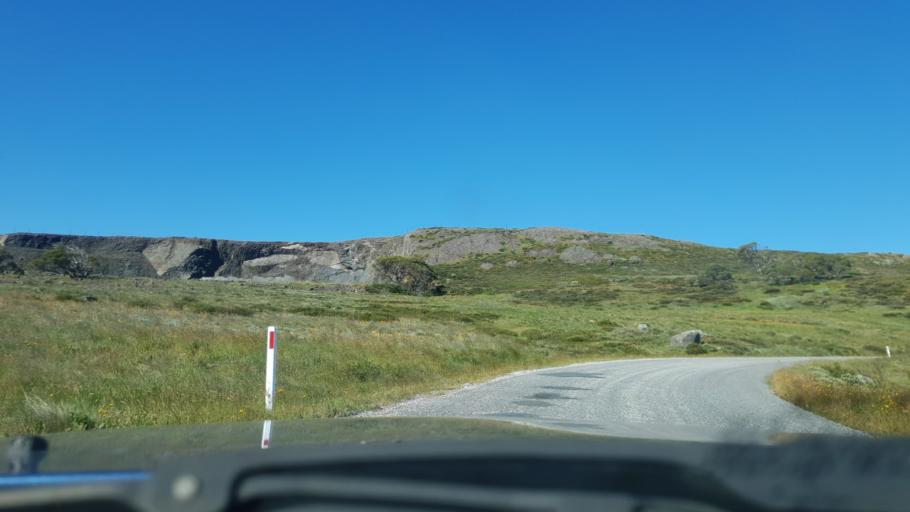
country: AU
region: Victoria
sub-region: Alpine
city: Mount Beauty
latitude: -36.8847
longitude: 147.3170
